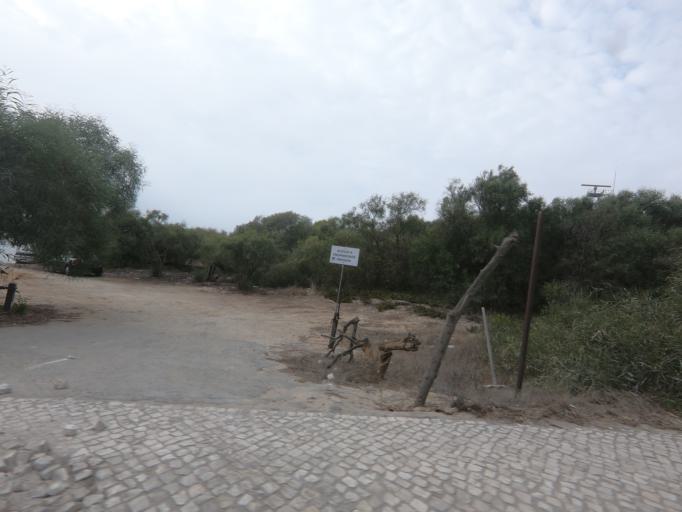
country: PT
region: Setubal
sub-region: Almada
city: Charneca
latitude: 38.5752
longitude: -9.1941
